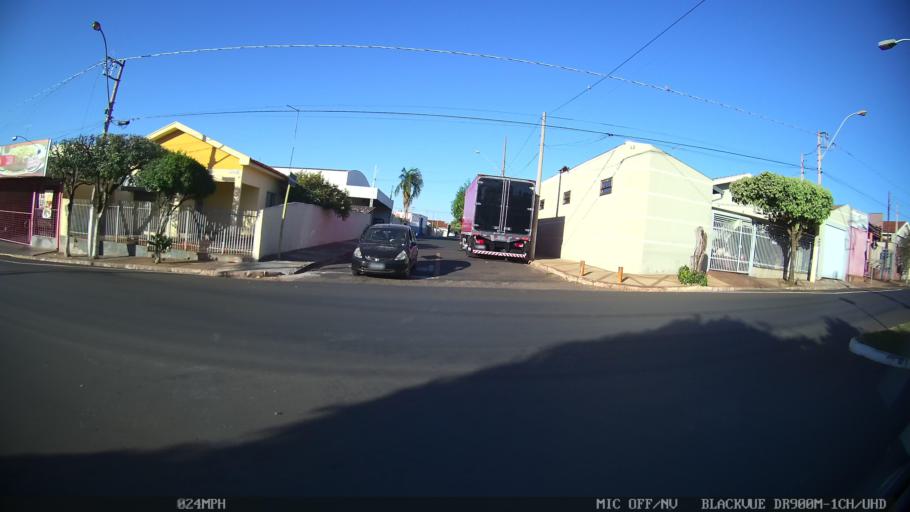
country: BR
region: Sao Paulo
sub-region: Guapiacu
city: Guapiacu
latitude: -20.7926
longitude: -49.2213
